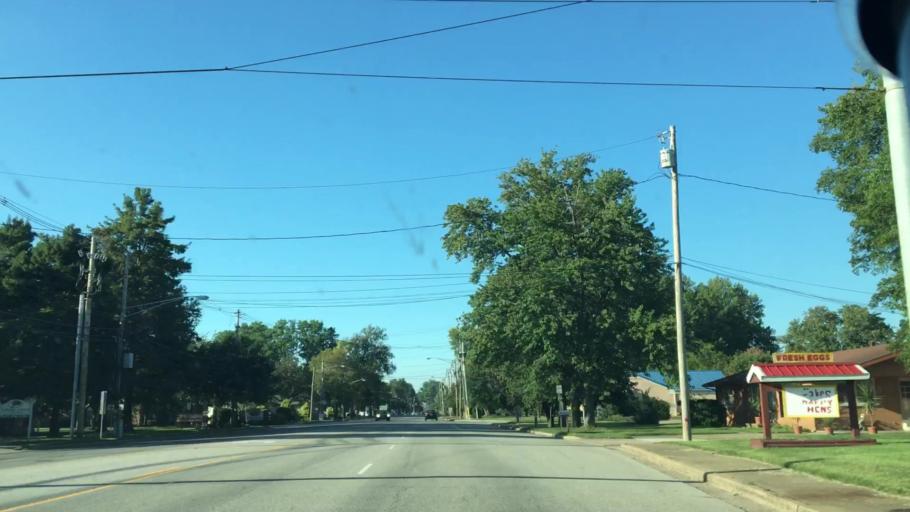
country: US
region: Indiana
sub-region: Vanderburgh County
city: Evansville
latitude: 37.9423
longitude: -87.4929
